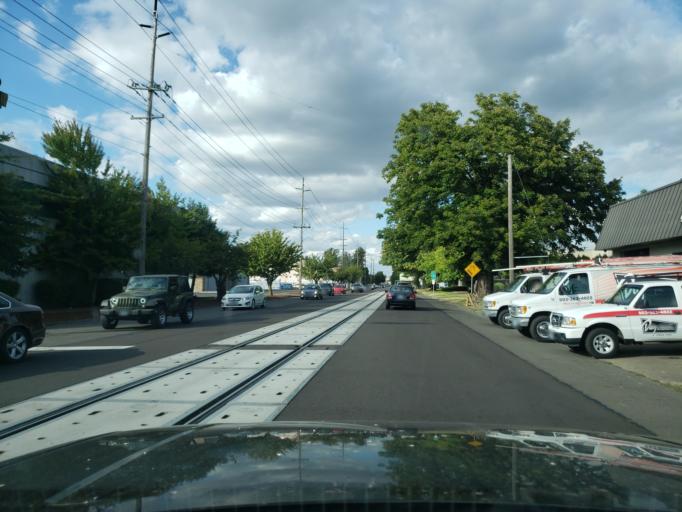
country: US
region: Oregon
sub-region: Marion County
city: Salem
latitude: 44.9475
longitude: -123.0387
